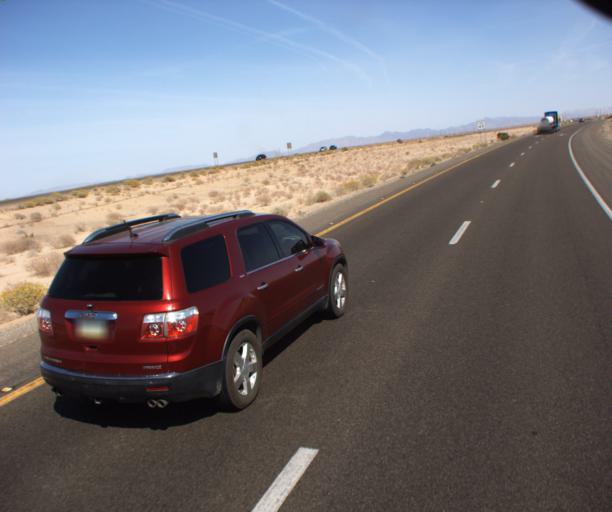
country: US
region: Arizona
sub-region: Yuma County
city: Somerton
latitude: 32.4960
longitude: -114.6545
